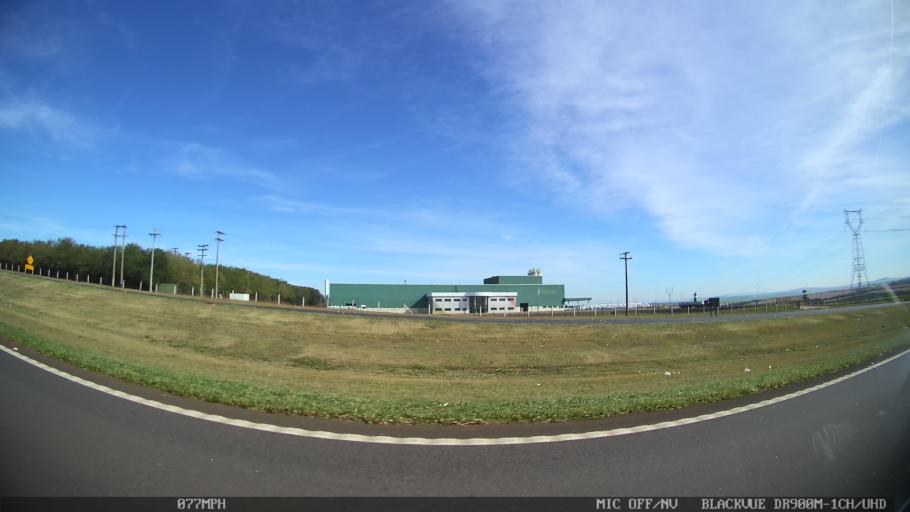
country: BR
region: Sao Paulo
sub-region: Cordeiropolis
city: Cordeiropolis
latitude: -22.4348
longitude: -47.3954
